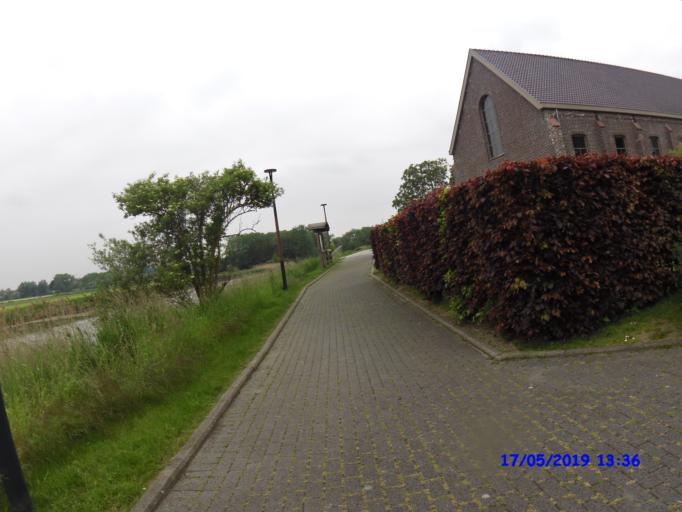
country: BE
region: Flanders
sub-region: Provincie West-Vlaanderen
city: Wielsbeke
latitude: 50.9085
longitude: 3.3905
